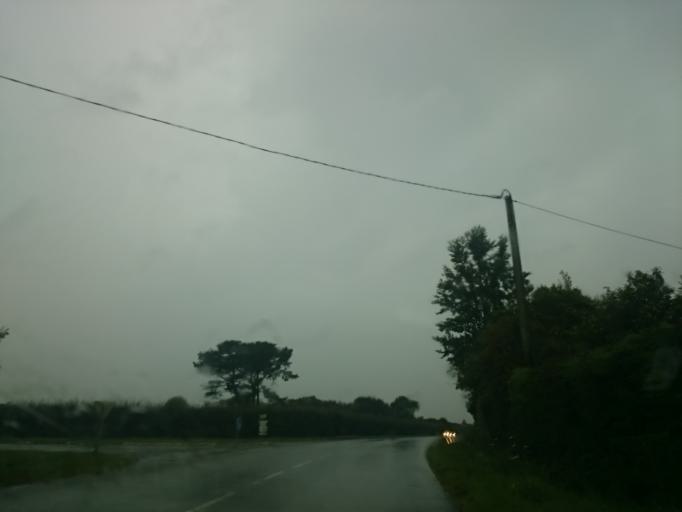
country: FR
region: Brittany
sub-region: Departement du Finistere
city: Plouvien
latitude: 48.5301
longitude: -4.4684
